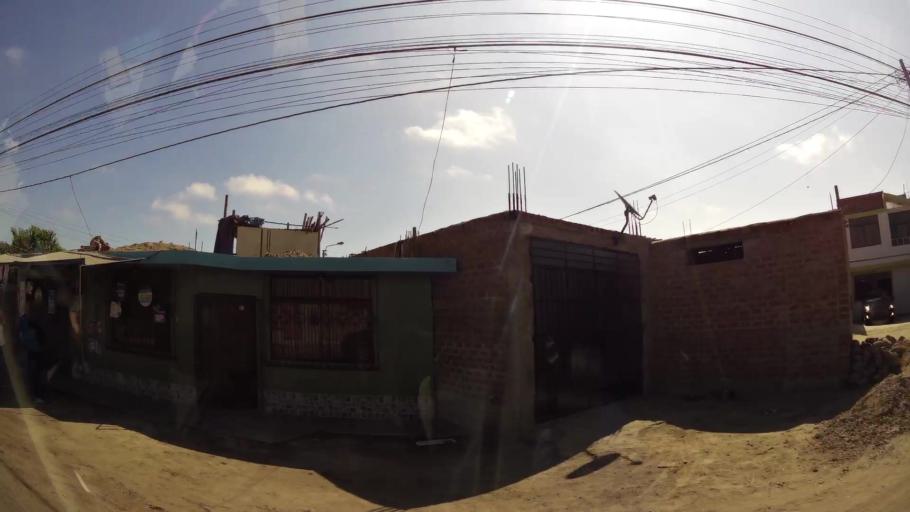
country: PE
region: Ica
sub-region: Provincia de Chincha
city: Sunampe
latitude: -13.4193
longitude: -76.1581
